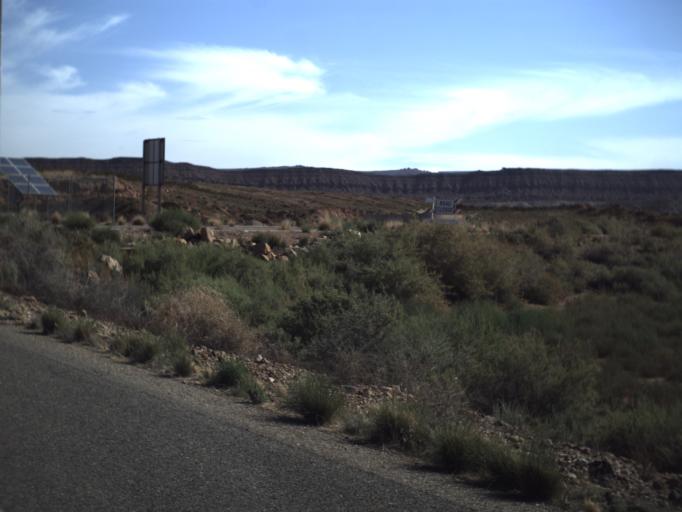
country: US
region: Utah
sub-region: Washington County
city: Washington
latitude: 37.0141
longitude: -113.4944
